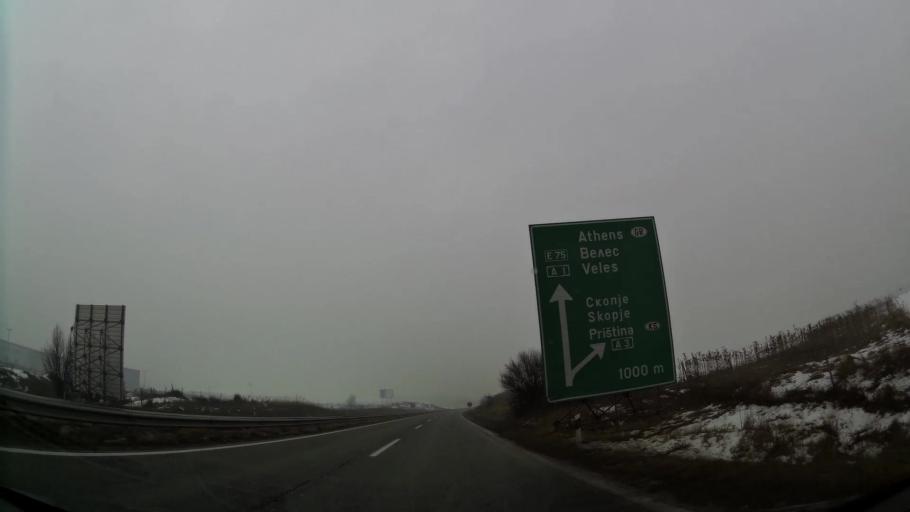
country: MK
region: Petrovec
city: Petrovec
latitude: 41.9488
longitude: 21.6308
